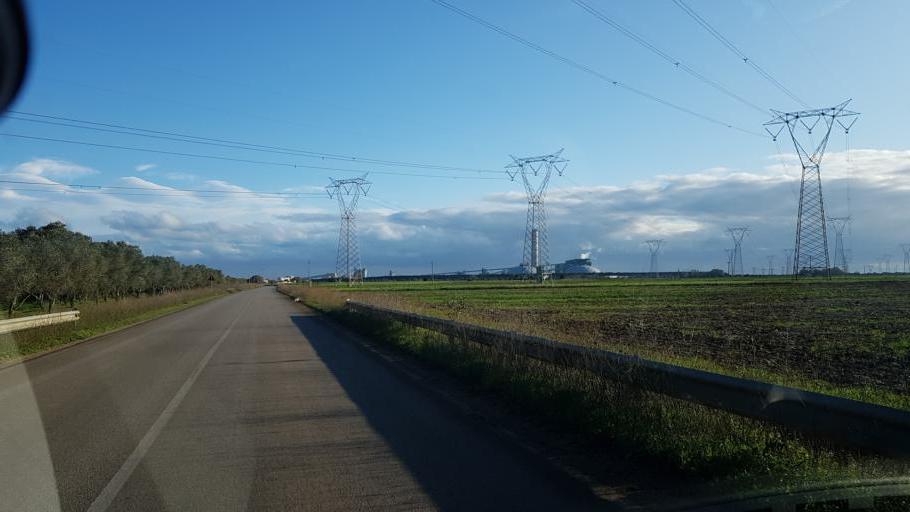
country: IT
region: Apulia
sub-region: Provincia di Brindisi
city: Tuturano
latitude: 40.5573
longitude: 18.0010
